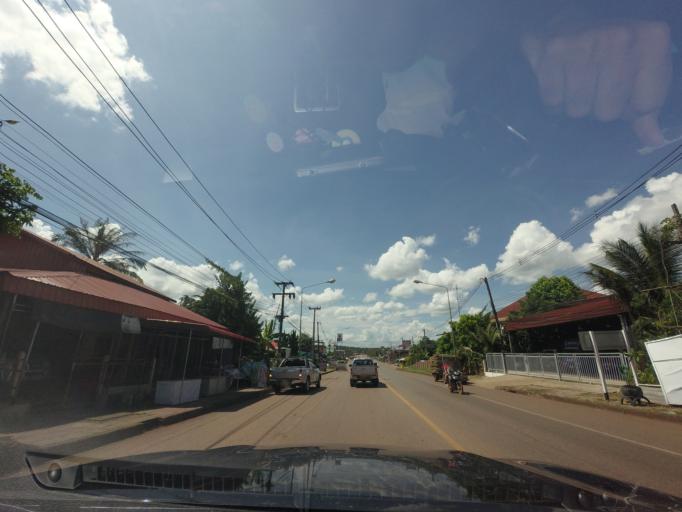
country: TH
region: Changwat Udon Thani
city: Ban Dung
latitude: 17.7018
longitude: 103.2574
